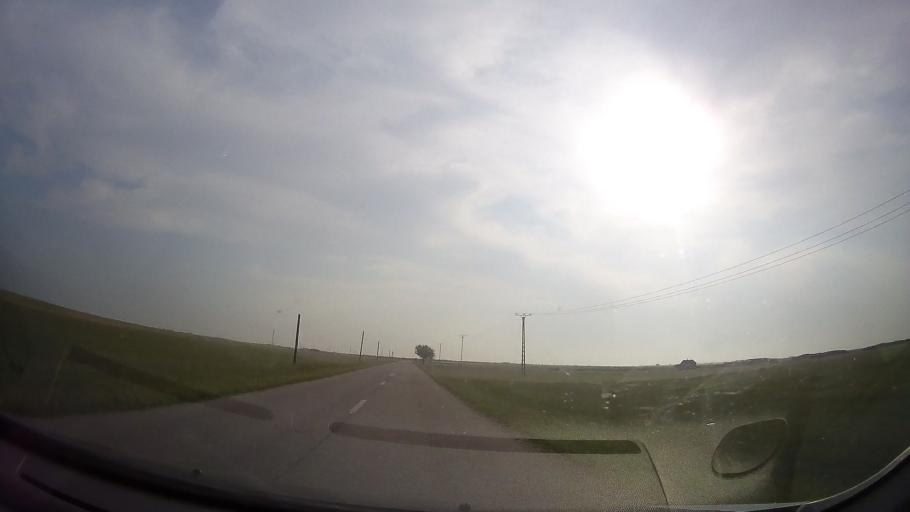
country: RO
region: Timis
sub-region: Comuna Foeni
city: Foeni
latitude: 45.5082
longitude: 20.8868
